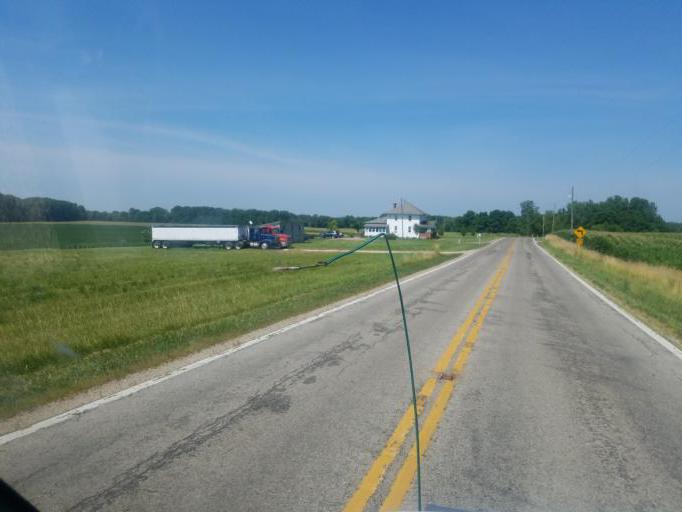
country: US
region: Ohio
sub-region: Champaign County
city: North Lewisburg
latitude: 40.2299
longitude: -83.5106
